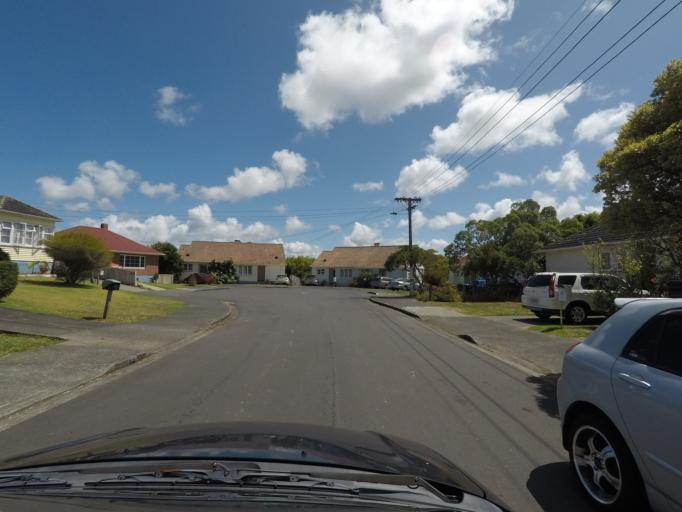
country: NZ
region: Auckland
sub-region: Auckland
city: Auckland
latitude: -36.8595
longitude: 174.7212
